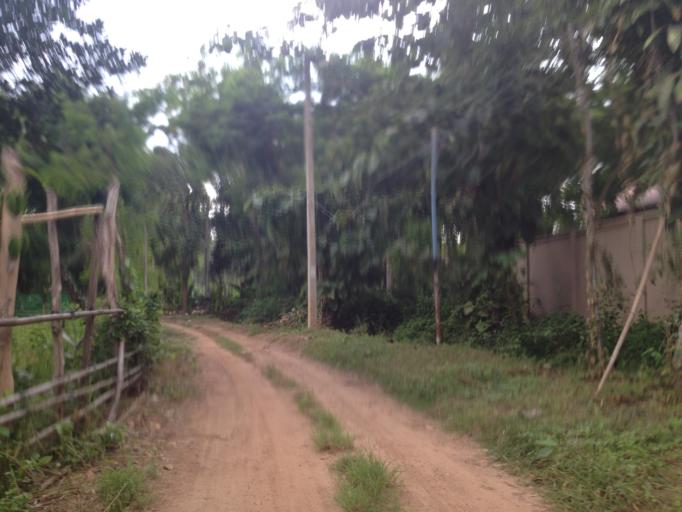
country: TH
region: Chiang Mai
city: Hang Dong
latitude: 18.7131
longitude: 98.9055
